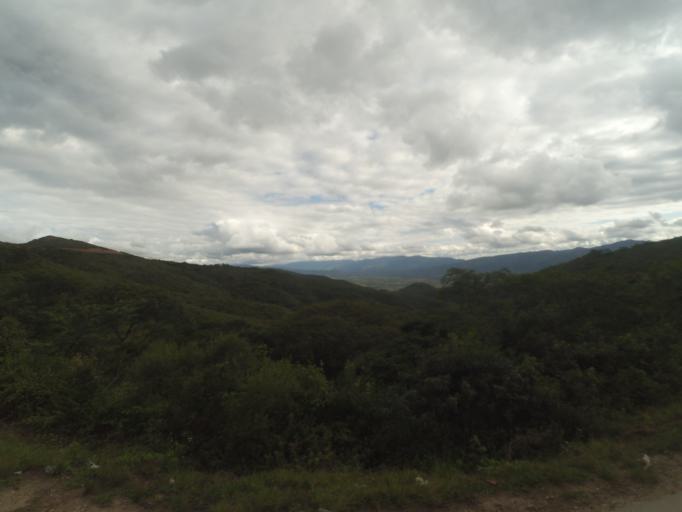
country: BO
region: Santa Cruz
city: Samaipata
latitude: -18.1766
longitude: -63.8701
